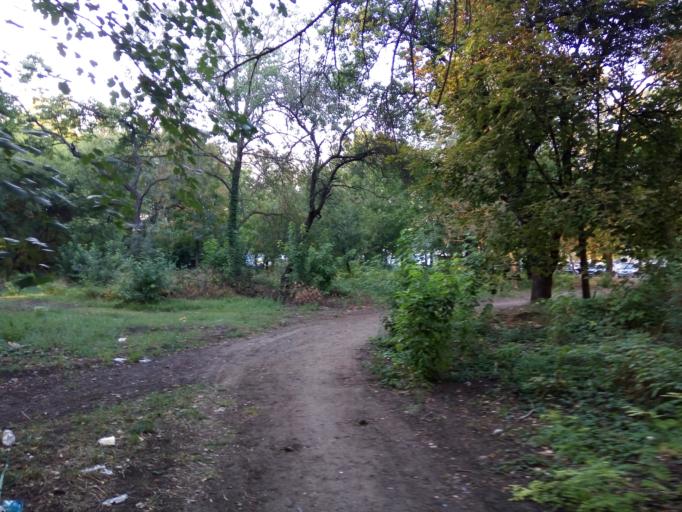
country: RU
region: Rostov
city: Rostov-na-Donu
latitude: 47.2429
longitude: 39.7586
